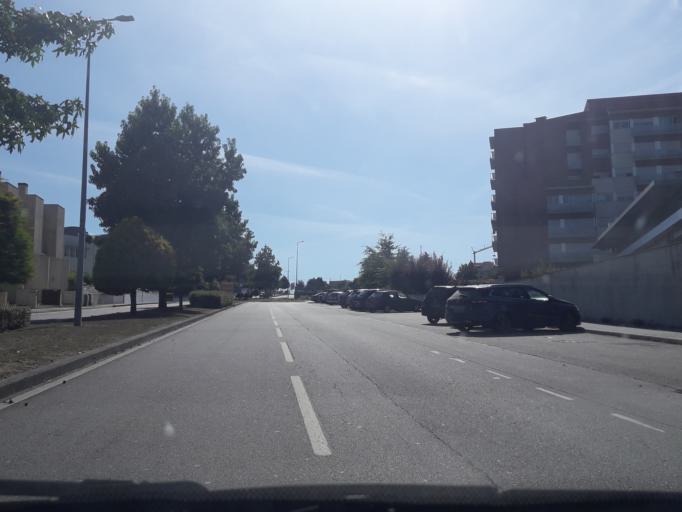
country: PT
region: Braga
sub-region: Braga
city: Braga
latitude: 41.5371
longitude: -8.4018
